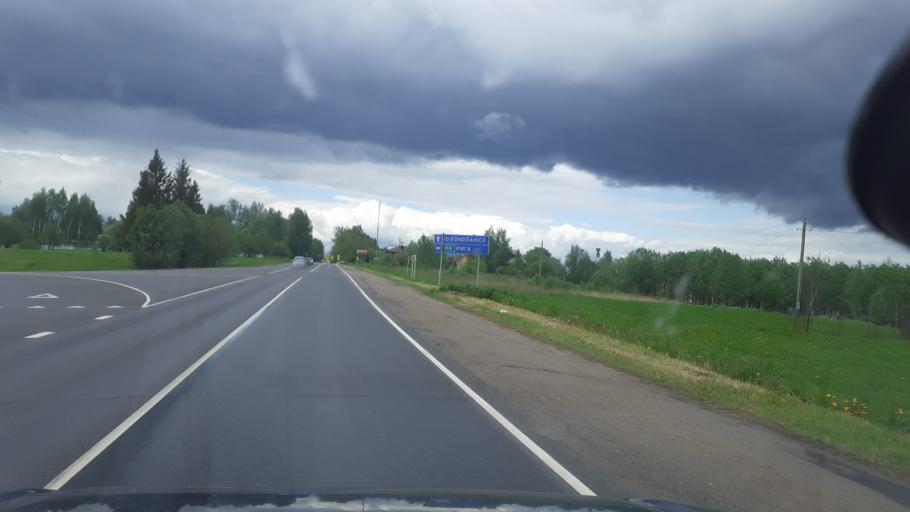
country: RU
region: Moskovskaya
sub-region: Volokolamskiy Rayon
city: Volokolamsk
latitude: 56.0236
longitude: 35.9659
